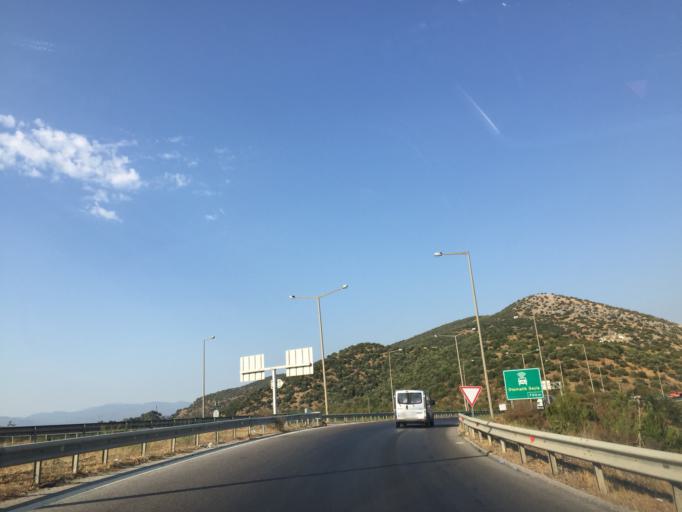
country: TR
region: Izmir
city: Belevi
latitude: 38.0311
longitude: 27.4445
